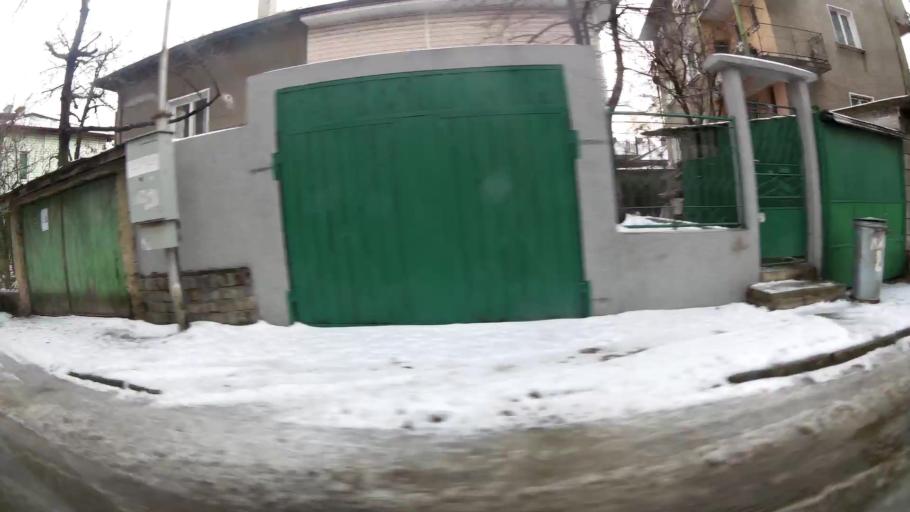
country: BG
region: Sofia-Capital
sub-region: Stolichna Obshtina
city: Sofia
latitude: 42.7249
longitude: 23.3304
